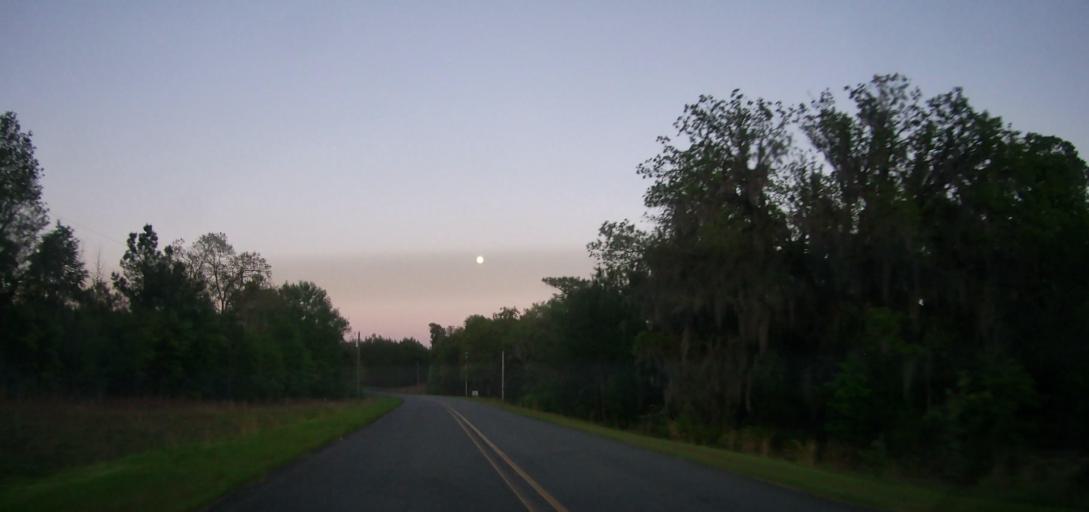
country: US
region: Georgia
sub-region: Marion County
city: Buena Vista
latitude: 32.2538
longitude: -84.6120
